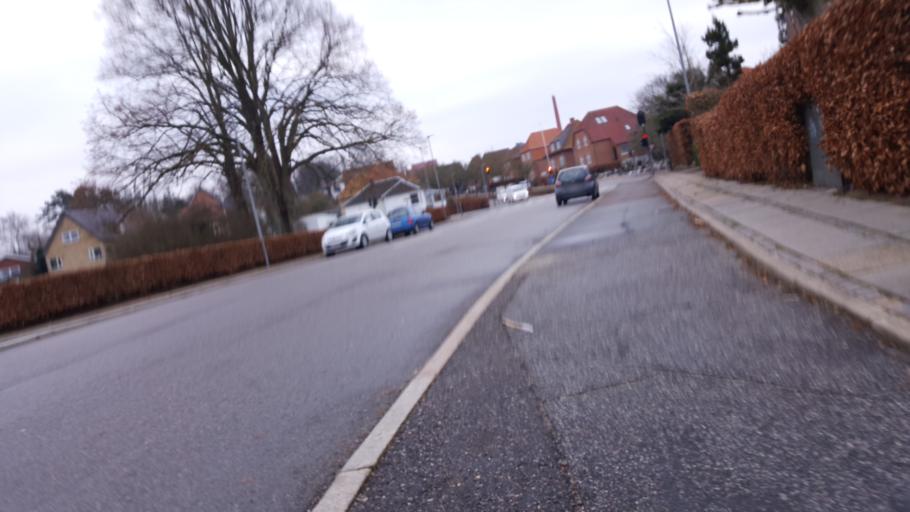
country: DK
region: South Denmark
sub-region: Kolding Kommune
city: Kolding
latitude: 55.4821
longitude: 9.4793
